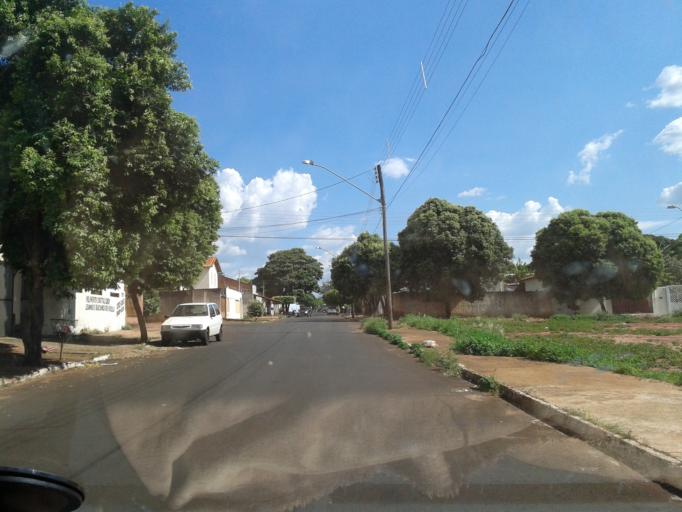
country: BR
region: Minas Gerais
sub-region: Ituiutaba
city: Ituiutaba
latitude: -18.9859
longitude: -49.4694
